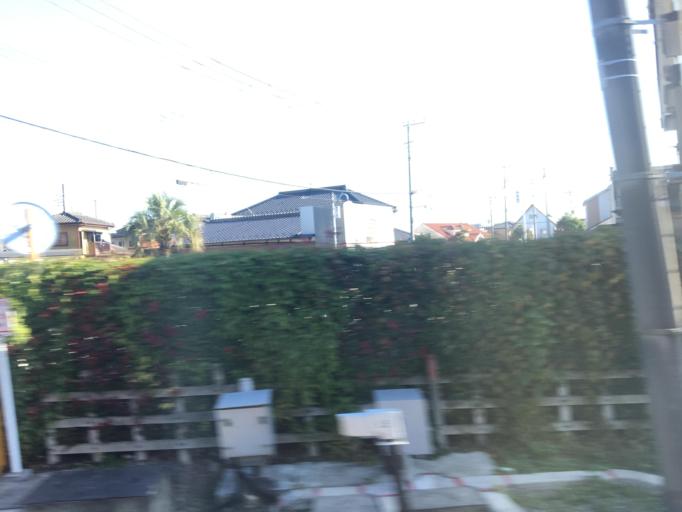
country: JP
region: Saitama
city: Hanyu
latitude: 36.1763
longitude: 139.5323
